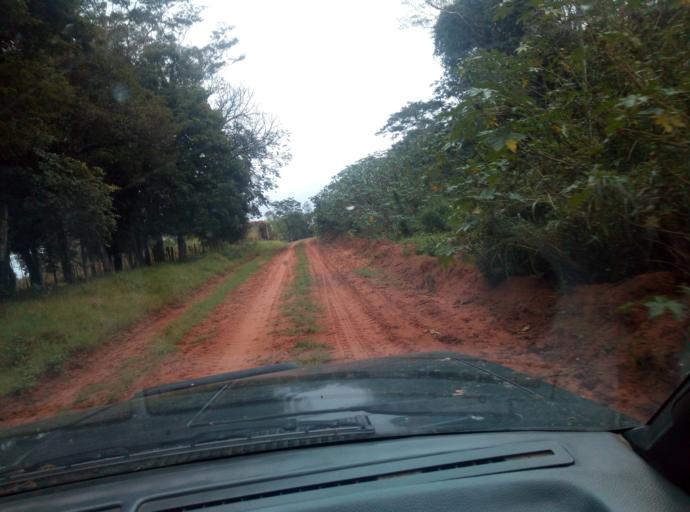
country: PY
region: Caaguazu
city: Carayao
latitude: -25.1917
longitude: -56.3421
